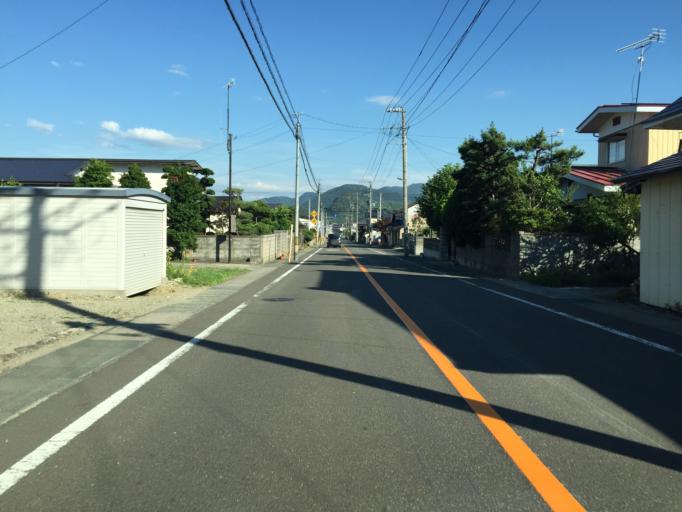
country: JP
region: Miyagi
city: Shiroishi
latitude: 37.9961
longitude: 140.4410
